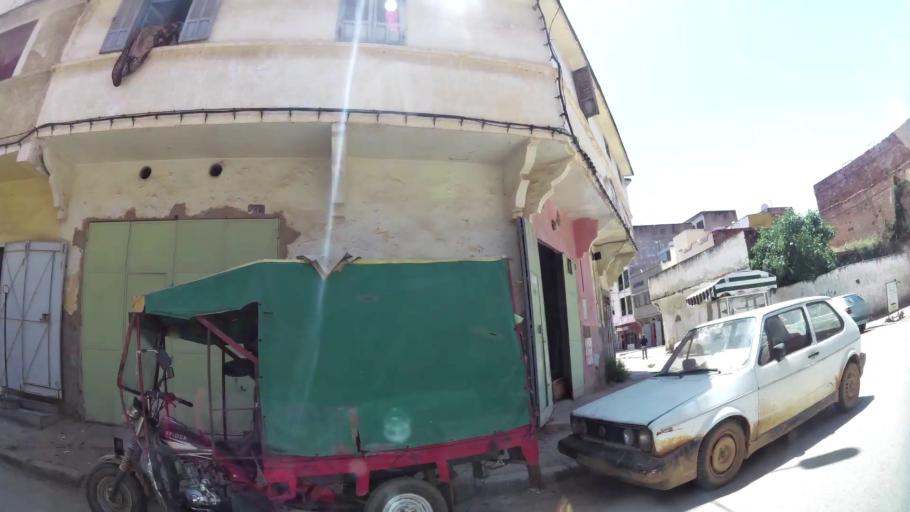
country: MA
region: Rabat-Sale-Zemmour-Zaer
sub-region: Khemisset
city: Khemisset
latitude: 33.8284
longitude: -6.0720
